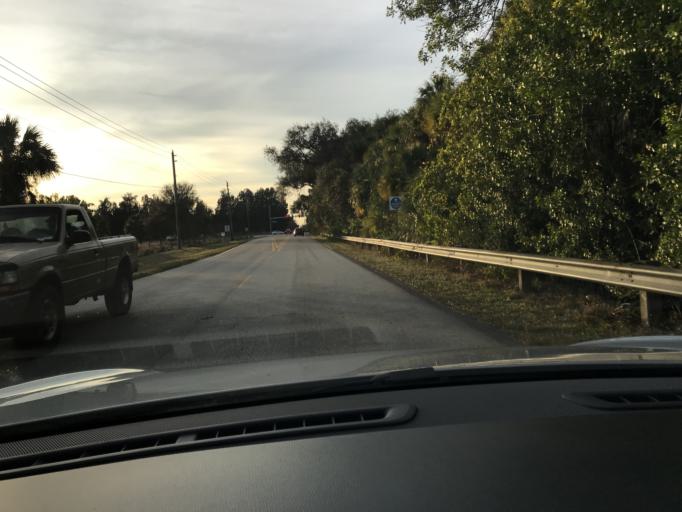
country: US
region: Florida
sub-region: Saint Lucie County
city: Lakewood Park
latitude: 27.4843
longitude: -80.3966
